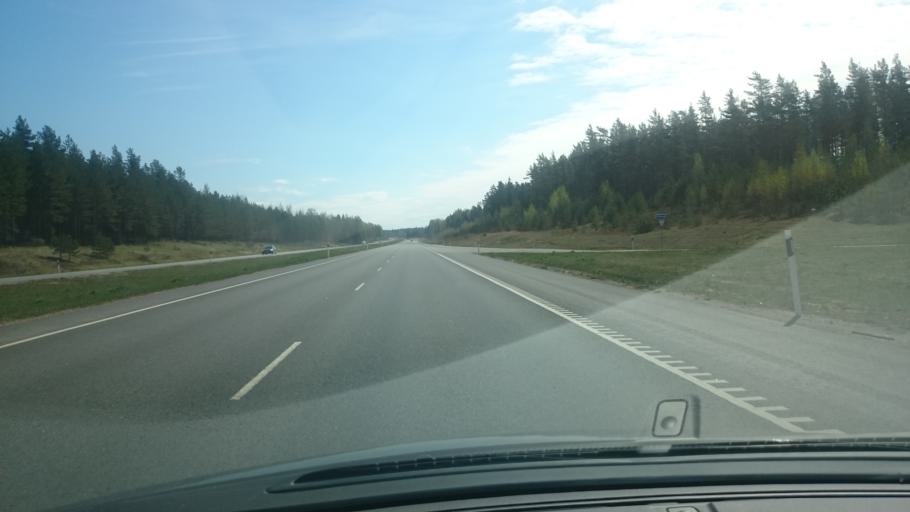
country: EE
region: Harju
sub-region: Loksa linn
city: Loksa
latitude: 59.4630
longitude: 25.7567
